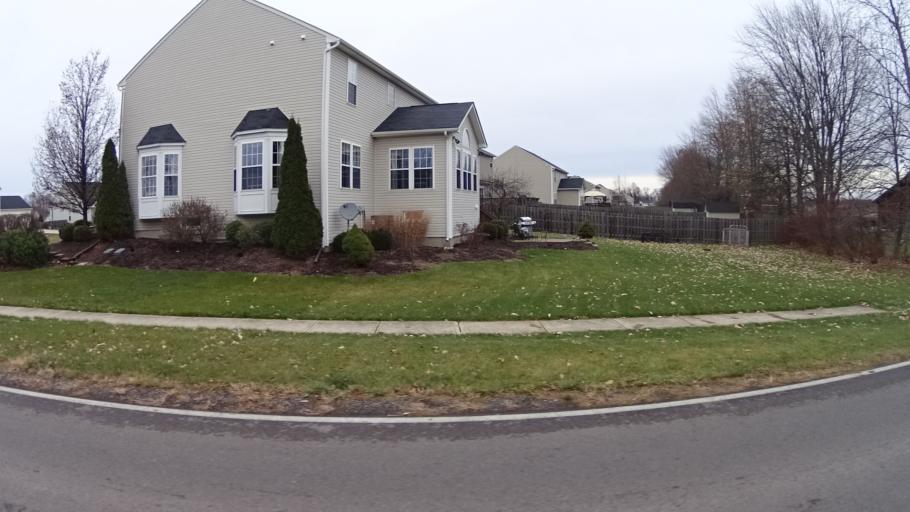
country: US
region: Ohio
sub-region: Lorain County
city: North Ridgeville
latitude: 41.3599
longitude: -82.0051
